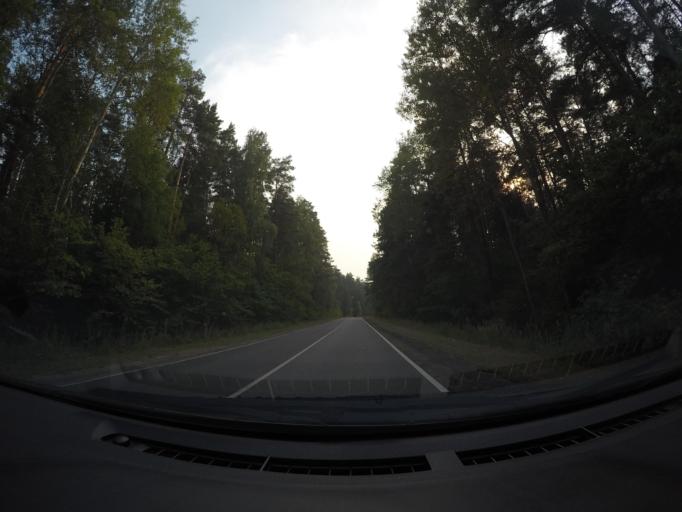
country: RU
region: Moskovskaya
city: Imeni Tsyurupy
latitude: 55.4990
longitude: 38.6966
